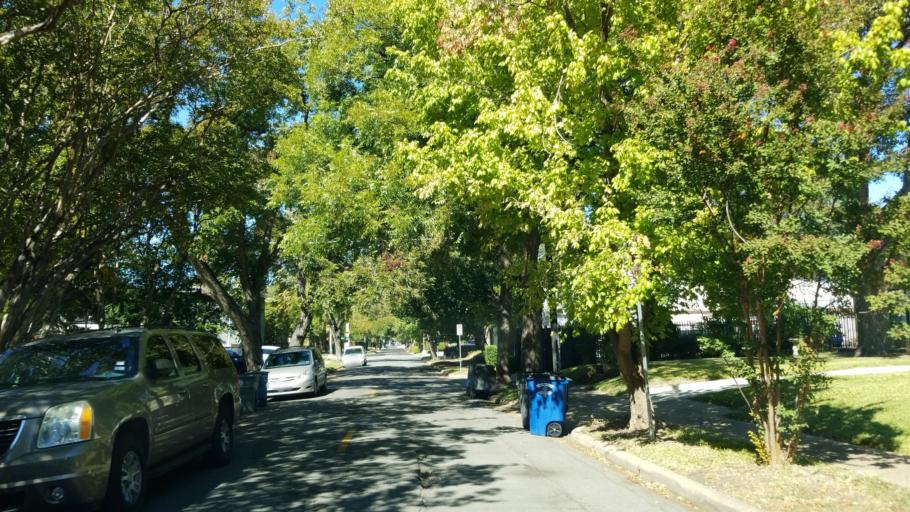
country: US
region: Texas
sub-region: Dallas County
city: Highland Park
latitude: 32.8082
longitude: -96.7579
